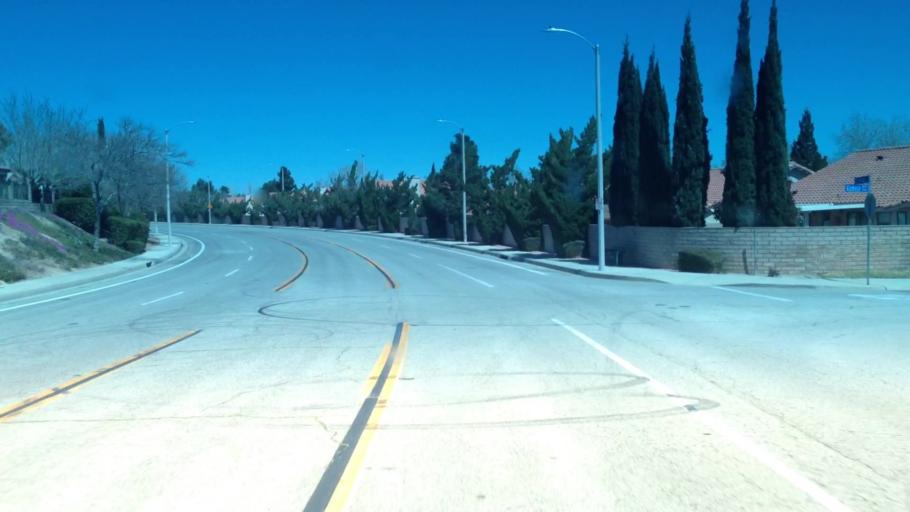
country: US
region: California
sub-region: Los Angeles County
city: Desert View Highlands
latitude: 34.5736
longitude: -118.1388
